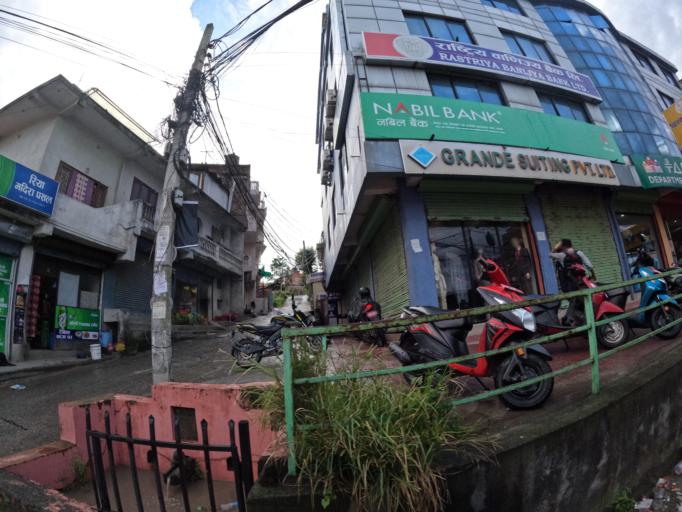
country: NP
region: Central Region
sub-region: Bagmati Zone
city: Kathmandu
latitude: 27.7447
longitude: 85.3229
